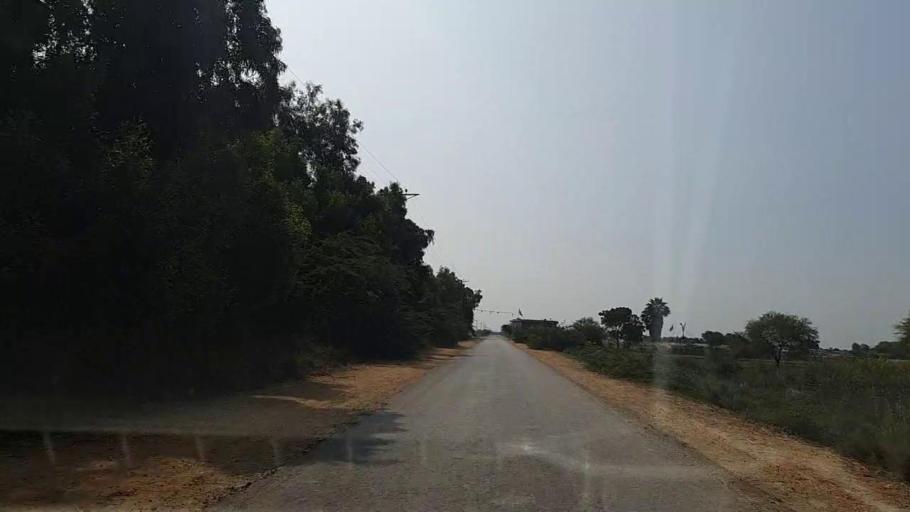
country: PK
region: Sindh
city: Chuhar Jamali
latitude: 24.3591
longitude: 67.9590
